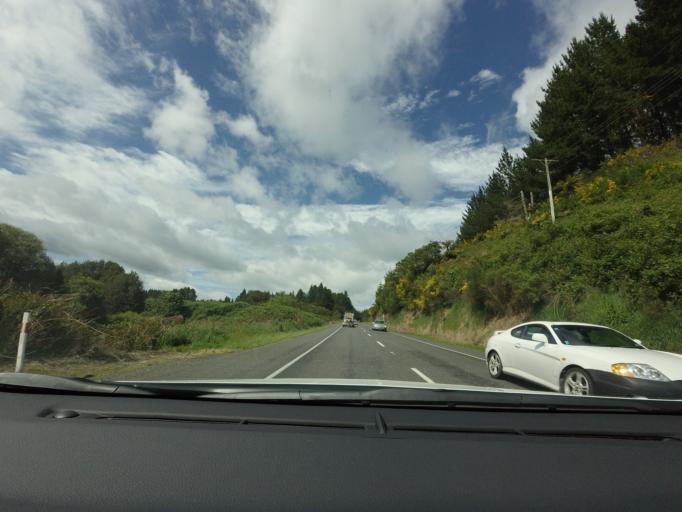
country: NZ
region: Bay of Plenty
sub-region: Rotorua District
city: Rotorua
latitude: -38.3221
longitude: 176.3724
